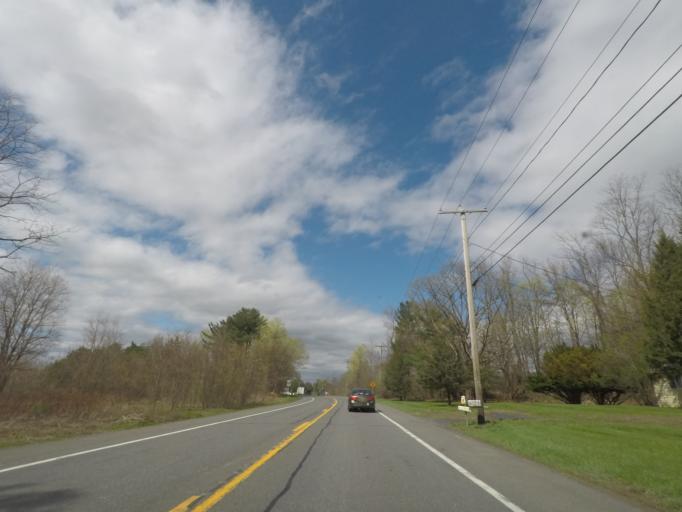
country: US
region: New York
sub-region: Columbia County
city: Niverville
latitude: 42.4667
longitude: -73.6905
